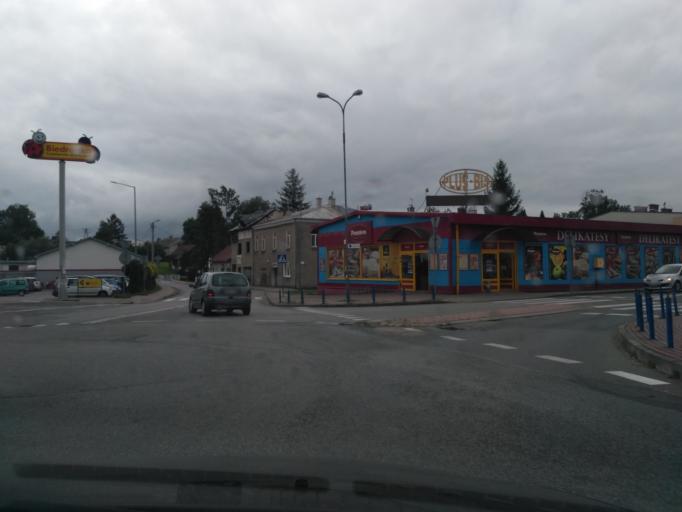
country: PL
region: Subcarpathian Voivodeship
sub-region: Powiat krosnienski
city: Korczyna
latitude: 49.7143
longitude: 21.8111
